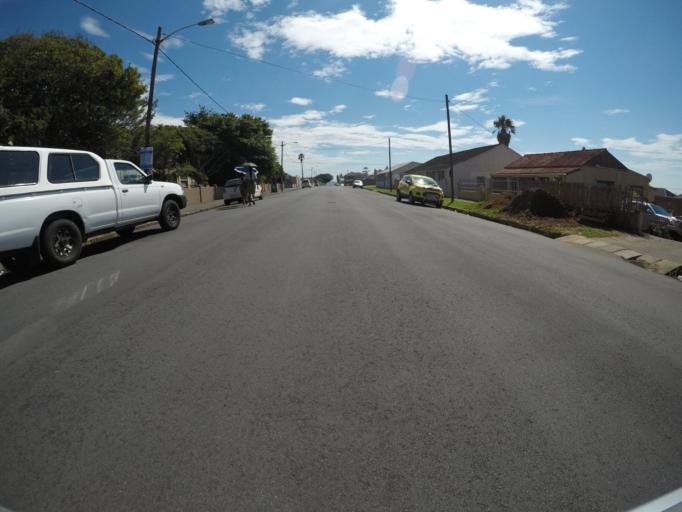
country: ZA
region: Eastern Cape
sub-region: Buffalo City Metropolitan Municipality
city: East London
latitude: -33.0340
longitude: 27.9064
